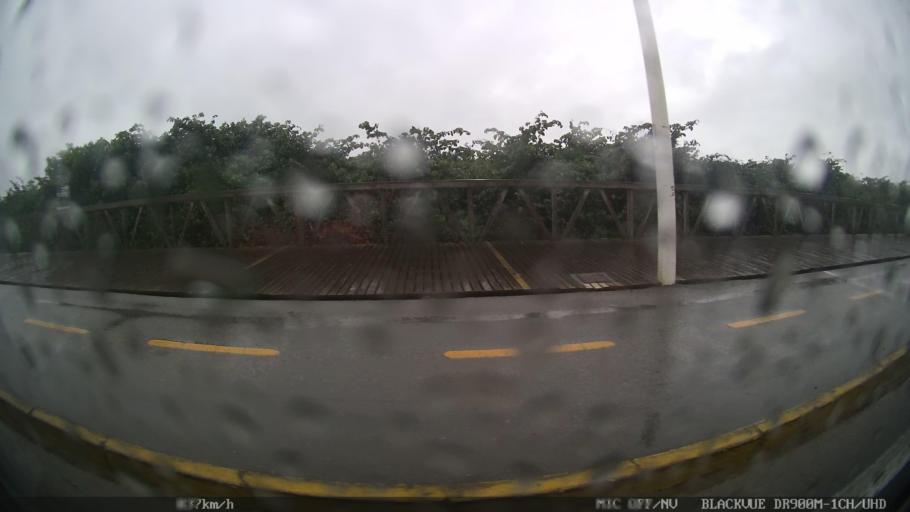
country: BR
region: Santa Catarina
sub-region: Navegantes
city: Navegantes
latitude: -26.8906
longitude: -48.6424
